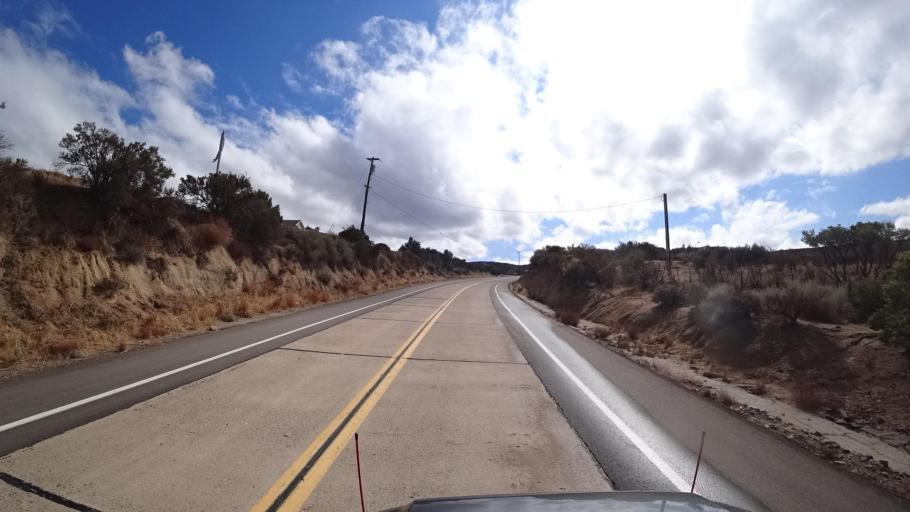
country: US
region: California
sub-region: San Diego County
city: Campo
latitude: 32.7253
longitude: -116.4163
